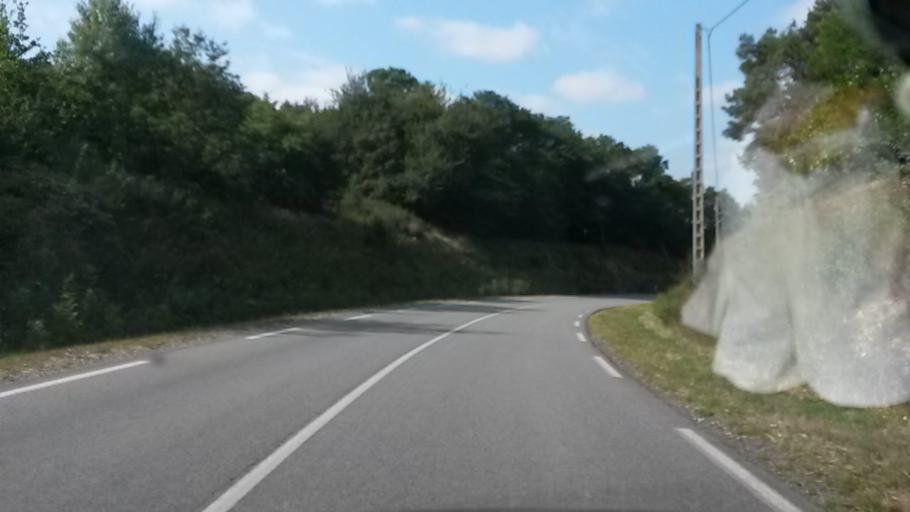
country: FR
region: Haute-Normandie
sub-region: Departement de l'Eure
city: Damville
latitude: 48.8476
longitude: 1.0517
